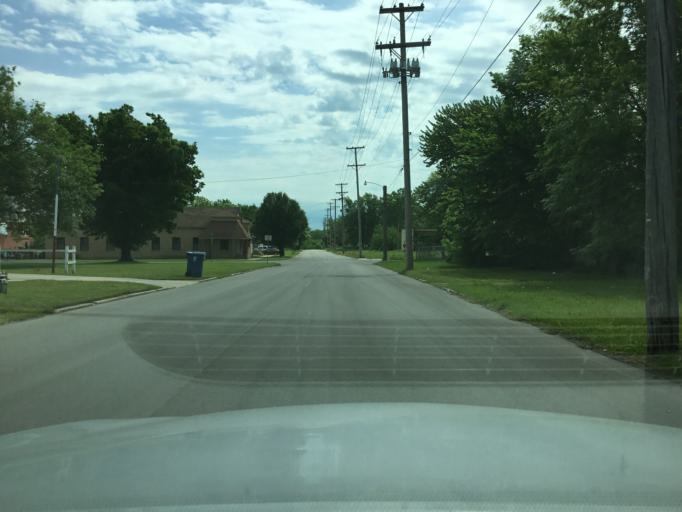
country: US
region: Kansas
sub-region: Montgomery County
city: Coffeyville
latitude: 37.0288
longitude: -95.6199
